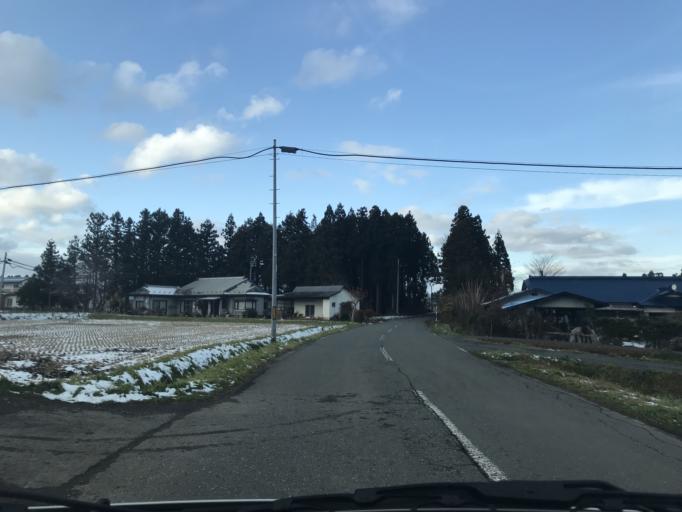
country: JP
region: Iwate
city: Kitakami
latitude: 39.2119
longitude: 141.0496
